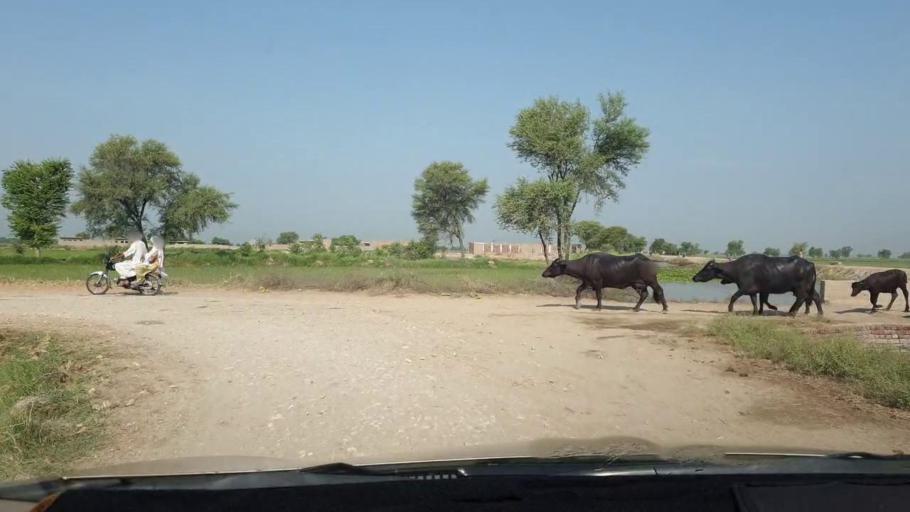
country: PK
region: Sindh
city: Larkana
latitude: 27.6417
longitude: 68.2295
